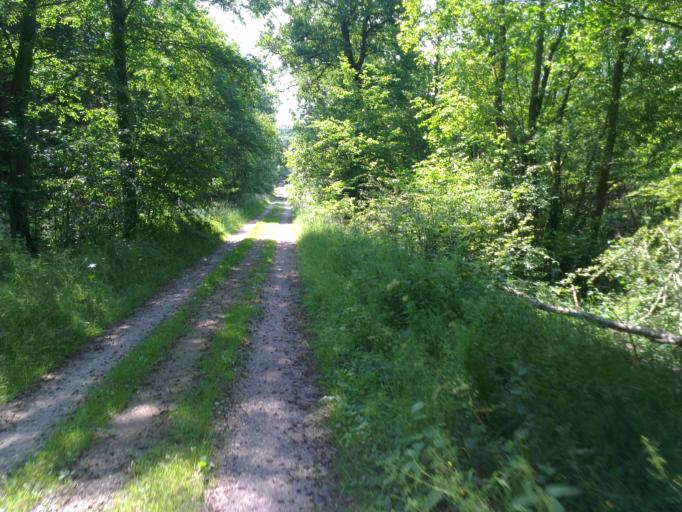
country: DK
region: Capital Region
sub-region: Allerod Kommune
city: Lillerod
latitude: 55.9200
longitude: 12.3603
